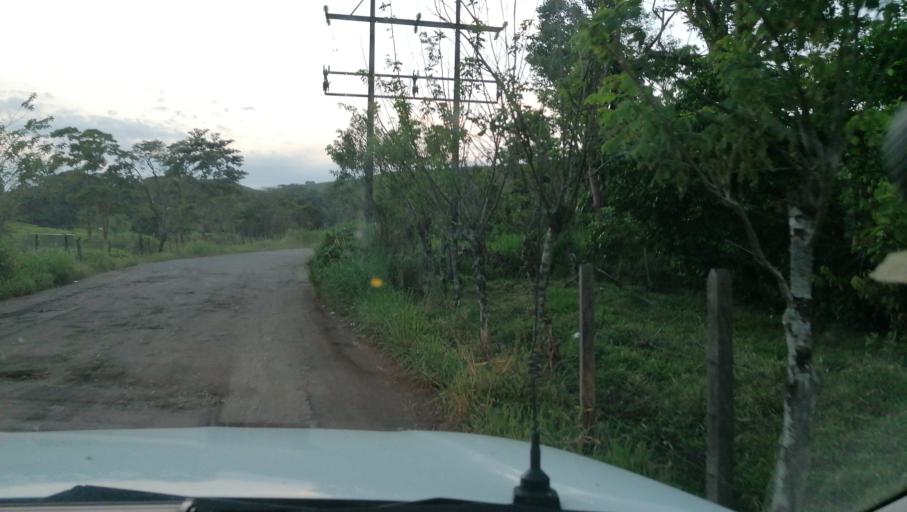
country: MX
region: Chiapas
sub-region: Ostuacan
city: Nuevo Juan del Grijalva
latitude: 17.4434
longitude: -93.3540
